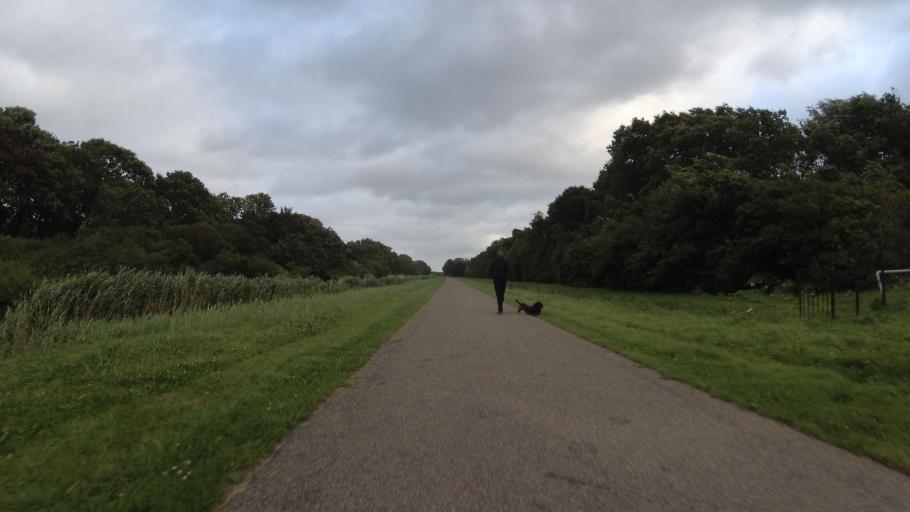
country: NL
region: North Holland
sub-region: Gemeente Den Helder
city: Den Helder
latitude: 52.9563
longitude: 4.7438
